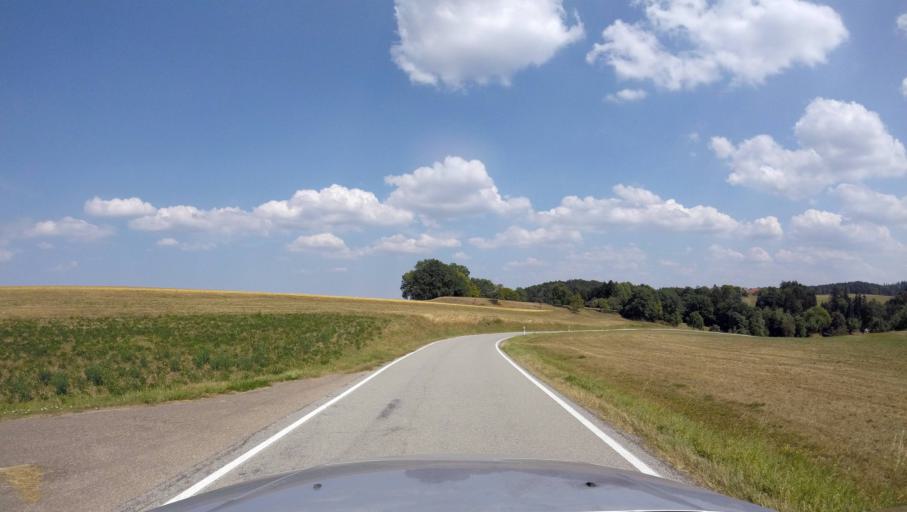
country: DE
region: Baden-Wuerttemberg
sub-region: Regierungsbezirk Stuttgart
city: Althutte
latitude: 48.9475
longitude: 9.5936
